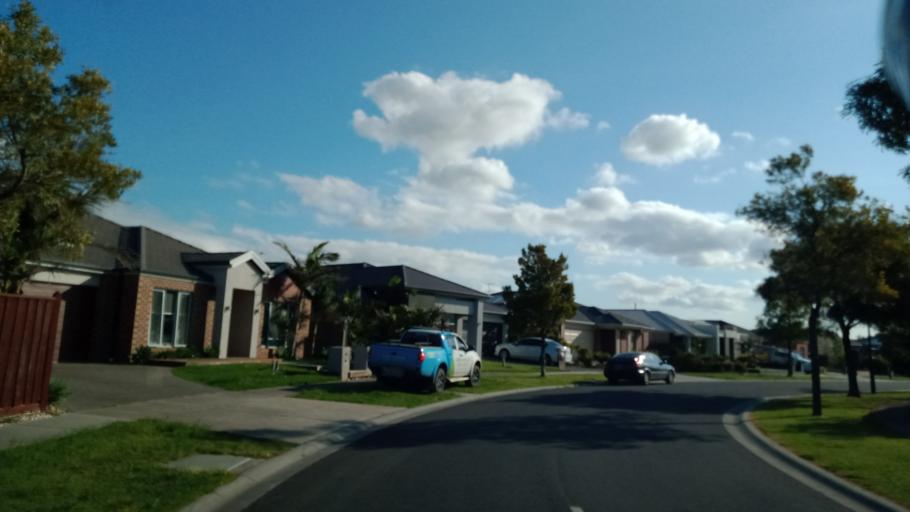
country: AU
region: Victoria
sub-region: Casey
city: Lynbrook
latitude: -38.0755
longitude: 145.2495
